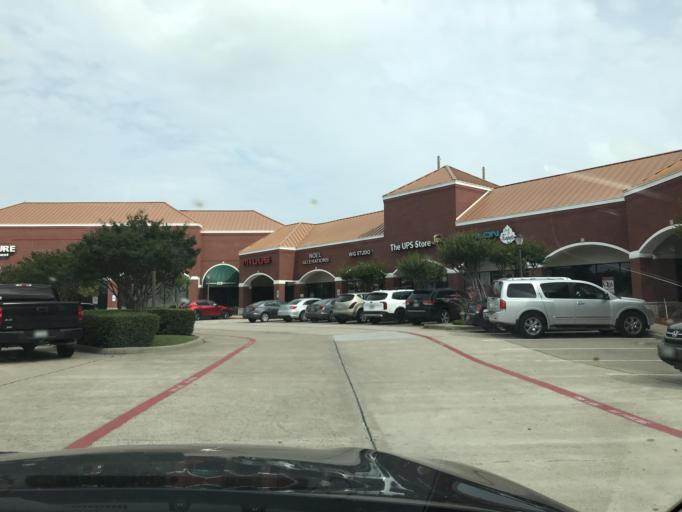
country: US
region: Texas
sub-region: Tarrant County
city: Benbrook
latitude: 32.6590
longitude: -97.4030
